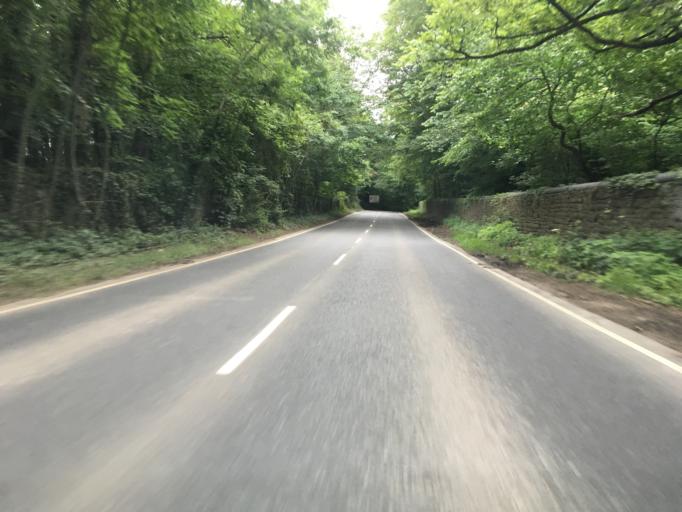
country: GB
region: England
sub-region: North Somerset
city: Long Ashton
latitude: 51.4535
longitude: -2.6493
